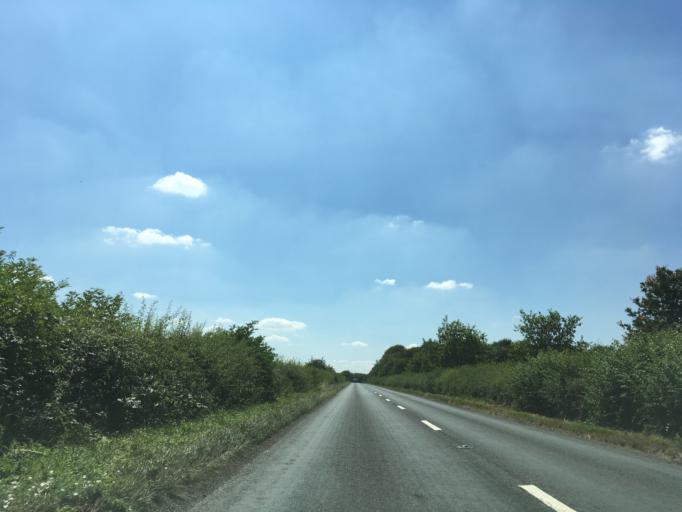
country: GB
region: England
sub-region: Gloucestershire
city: Tetbury
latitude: 51.6568
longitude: -2.1266
